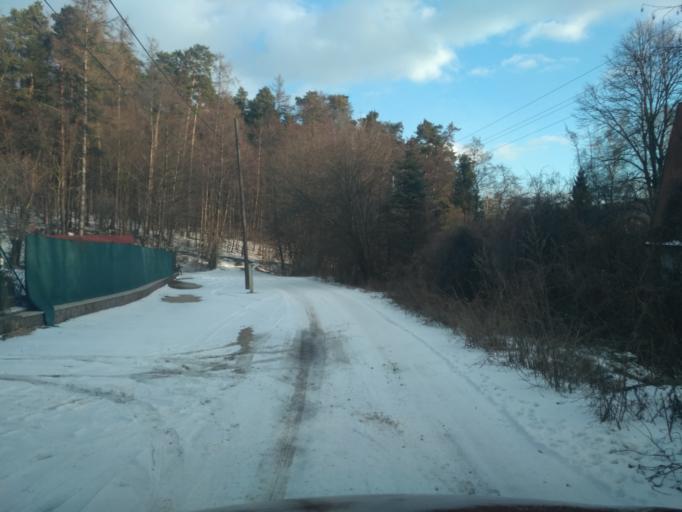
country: SK
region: Kosicky
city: Kosice
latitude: 48.7322
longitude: 21.1614
